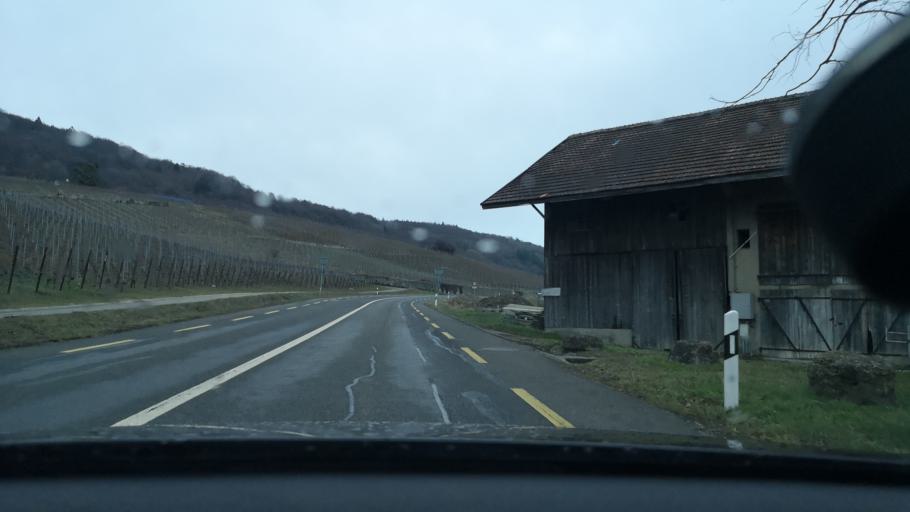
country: CH
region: Vaud
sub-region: Jura-Nord vaudois District
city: Yvonand
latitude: 46.8557
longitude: 6.7243
